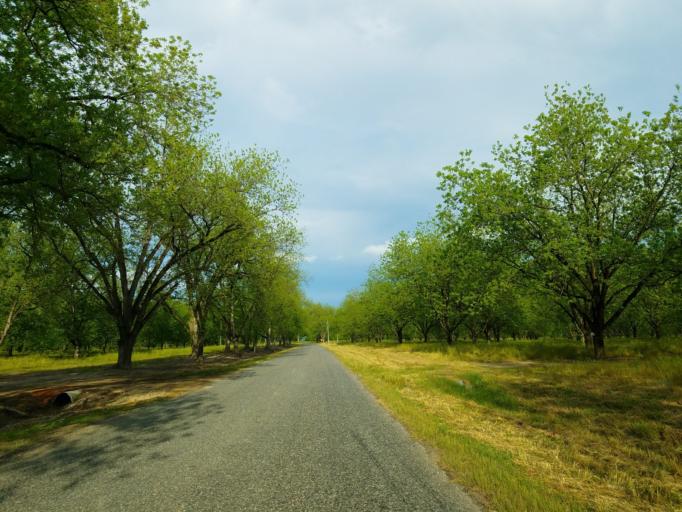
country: US
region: Georgia
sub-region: Dooly County
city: Vienna
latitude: 32.0420
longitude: -83.7900
